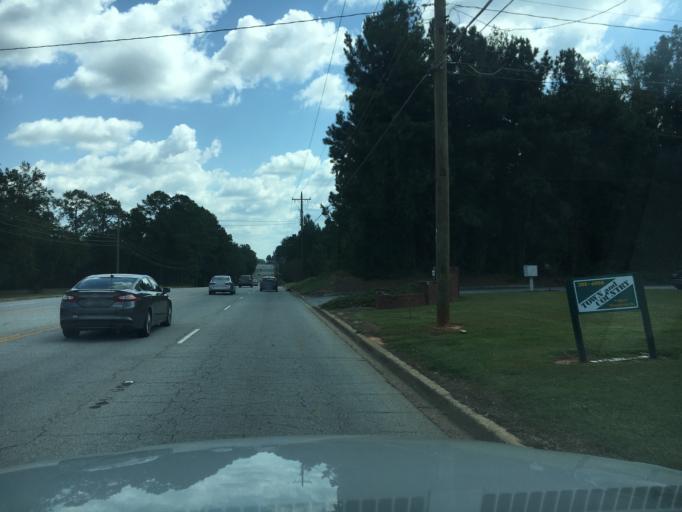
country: US
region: South Carolina
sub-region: Greenwood County
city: Greenwood
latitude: 34.2339
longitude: -82.2045
